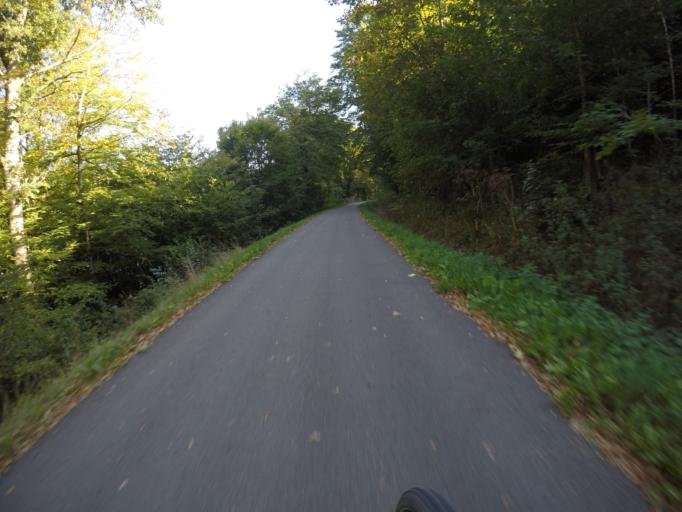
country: DE
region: Baden-Wuerttemberg
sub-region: Regierungsbezirk Stuttgart
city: Waldenbuch
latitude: 48.6377
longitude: 9.1699
